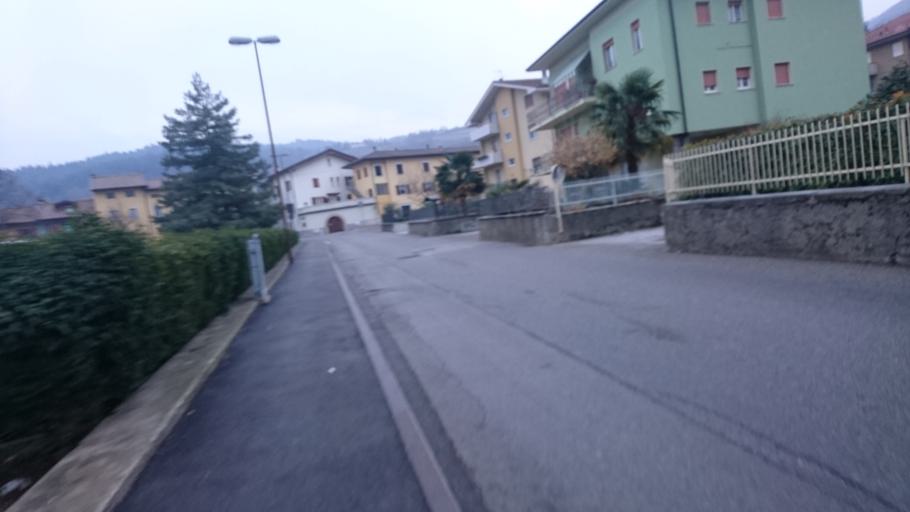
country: IT
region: Trentino-Alto Adige
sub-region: Provincia di Trento
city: Mori
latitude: 45.8465
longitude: 10.9782
